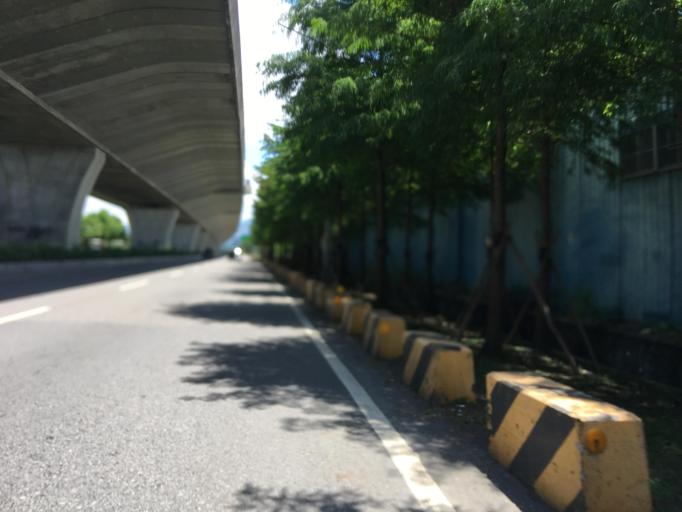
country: TW
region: Taiwan
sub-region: Yilan
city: Yilan
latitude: 24.6876
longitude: 121.7914
